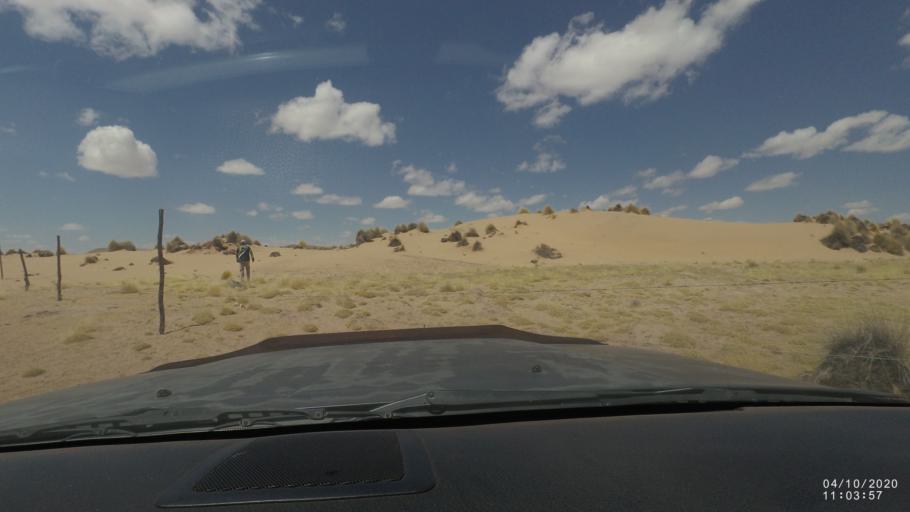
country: BO
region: Oruro
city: Poopo
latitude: -18.7025
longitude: -67.4683
